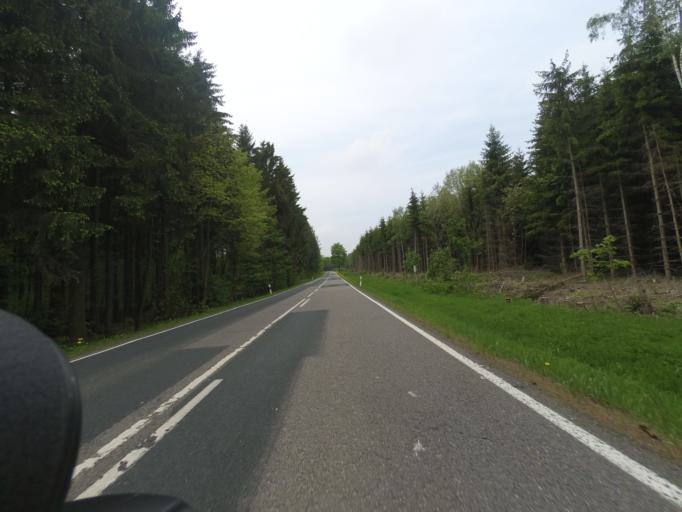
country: DE
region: Saxony
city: Grossruckerswalde
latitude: 50.6521
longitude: 13.1320
